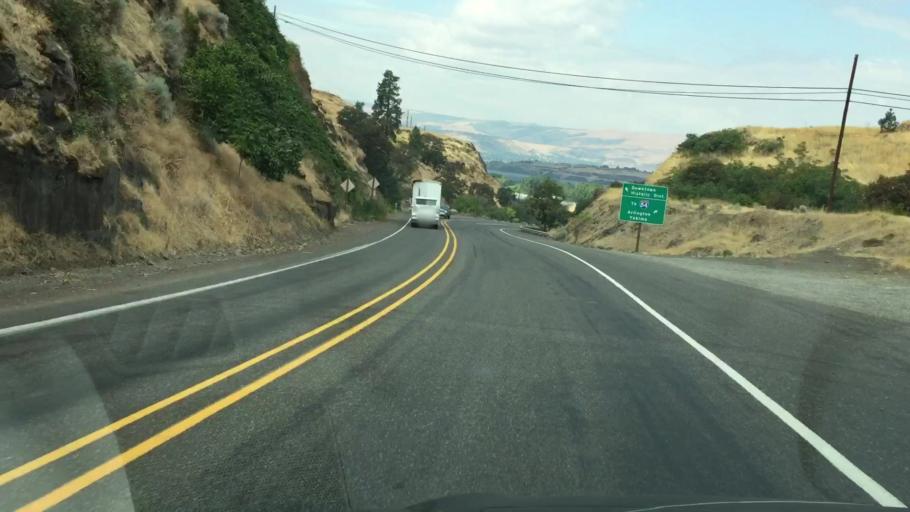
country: US
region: Oregon
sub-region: Wasco County
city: The Dalles
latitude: 45.5977
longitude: -121.1367
